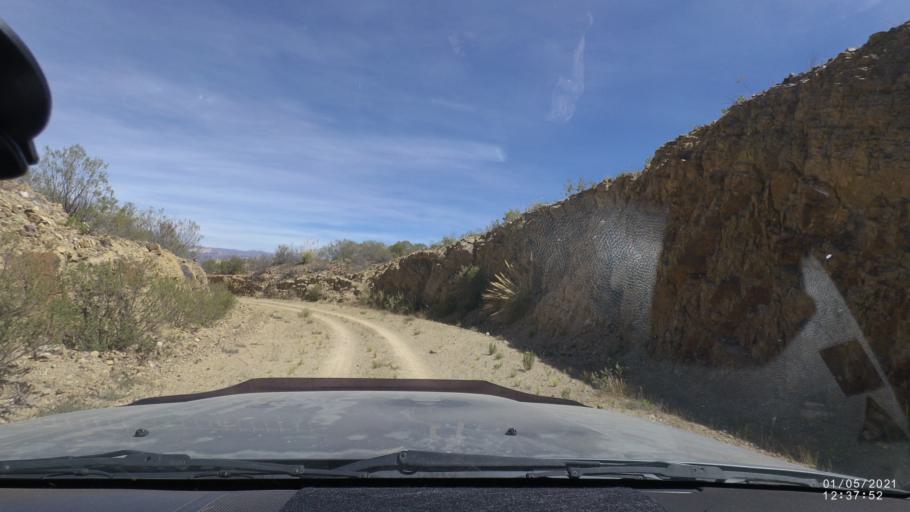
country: BO
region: Cochabamba
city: Capinota
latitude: -17.6787
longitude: -66.1577
